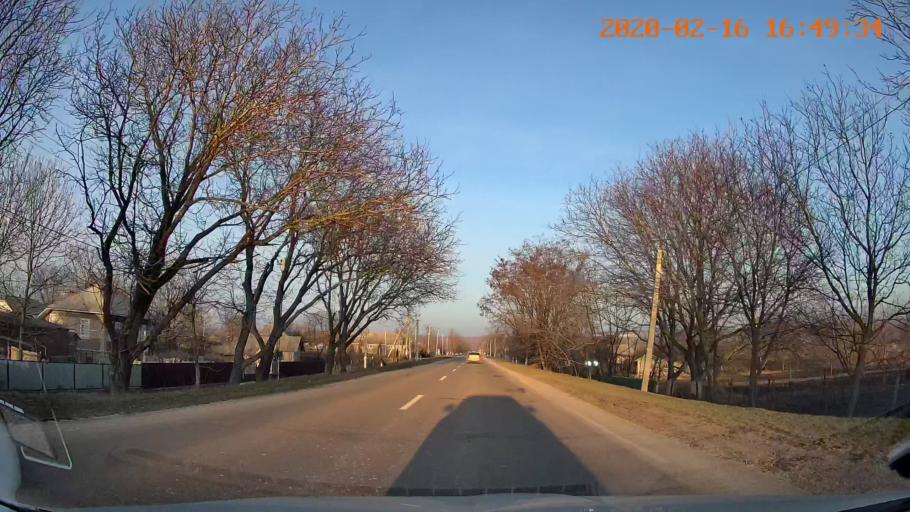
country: RO
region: Botosani
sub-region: Comuna Radauti-Prut
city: Miorcani
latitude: 48.2908
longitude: 26.9192
